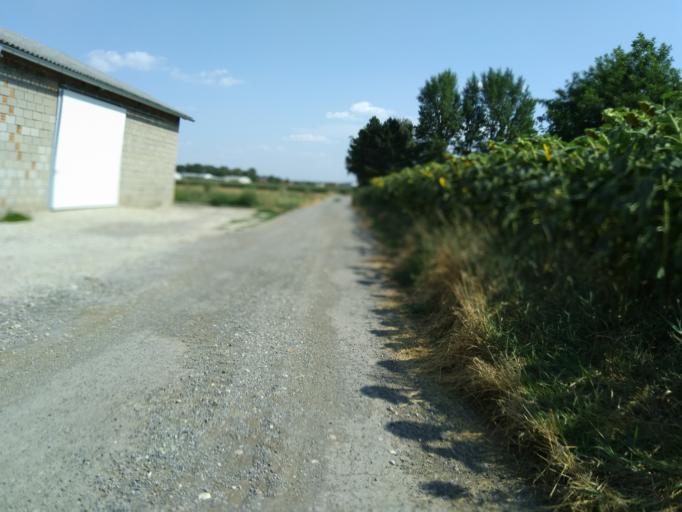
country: AT
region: Lower Austria
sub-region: Politischer Bezirk Ganserndorf
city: Gross-Schweinbarth
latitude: 48.4201
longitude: 16.6332
